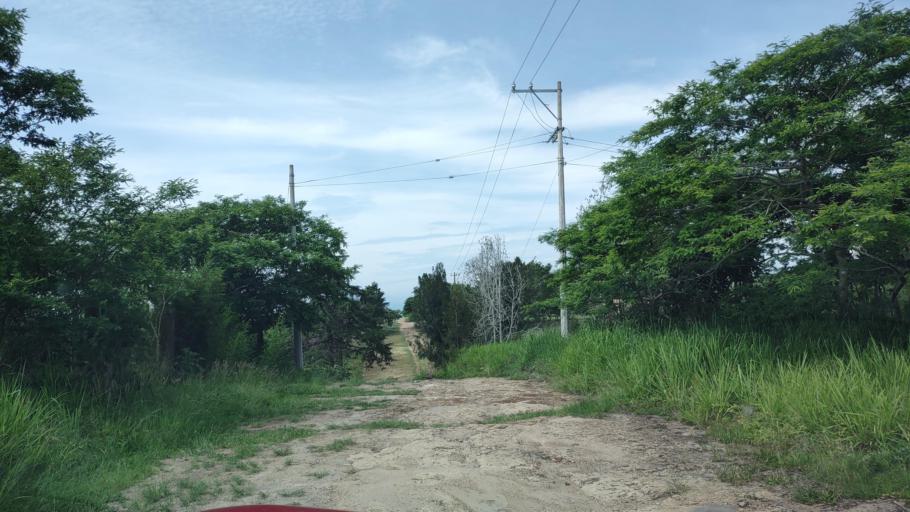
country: MX
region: Veracruz
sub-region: Emiliano Zapata
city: Dos Rios
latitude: 19.4718
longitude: -96.8267
